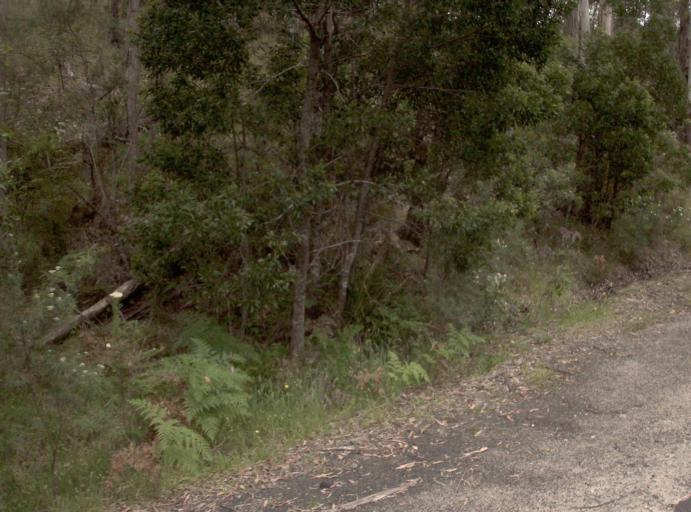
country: AU
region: New South Wales
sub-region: Bombala
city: Bombala
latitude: -37.3570
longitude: 149.2023
